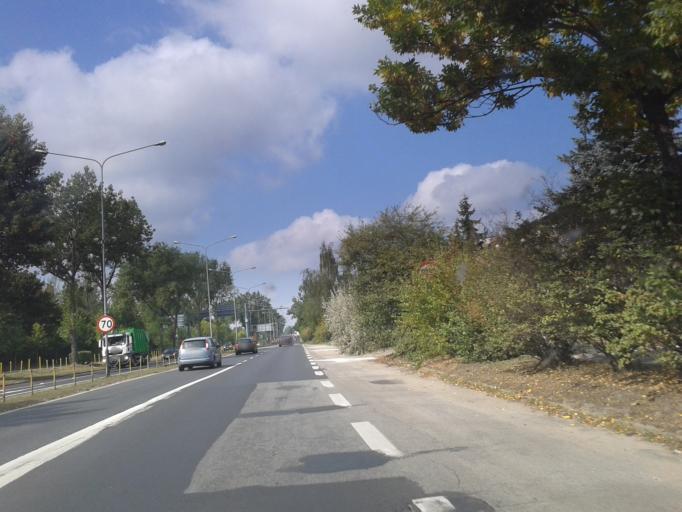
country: PL
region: Greater Poland Voivodeship
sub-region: Powiat poznanski
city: Suchy Las
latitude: 52.4225
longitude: 16.8696
